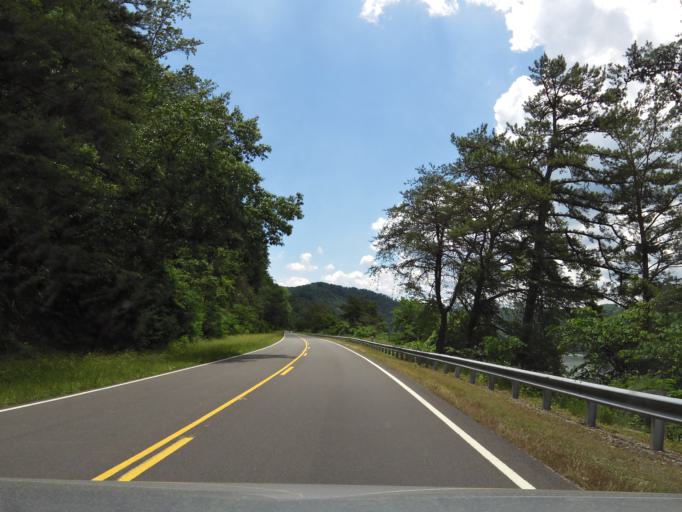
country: US
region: Tennessee
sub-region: Loudon County
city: Greenback
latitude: 35.5398
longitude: -83.9960
